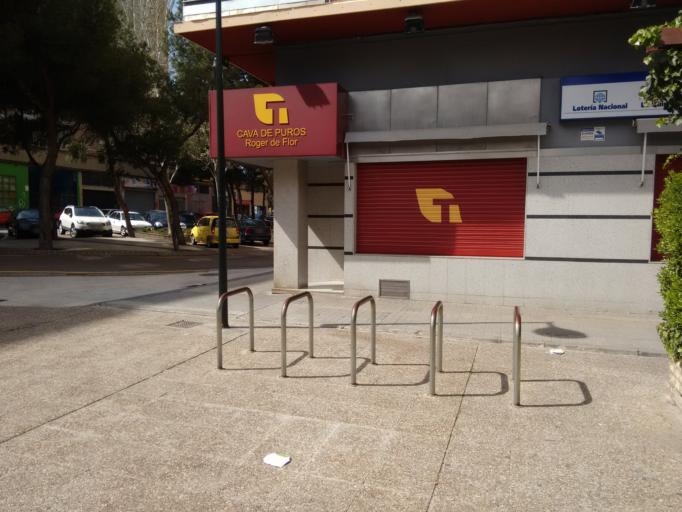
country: ES
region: Aragon
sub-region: Provincia de Zaragoza
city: Delicias
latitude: 41.6495
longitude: -0.9169
